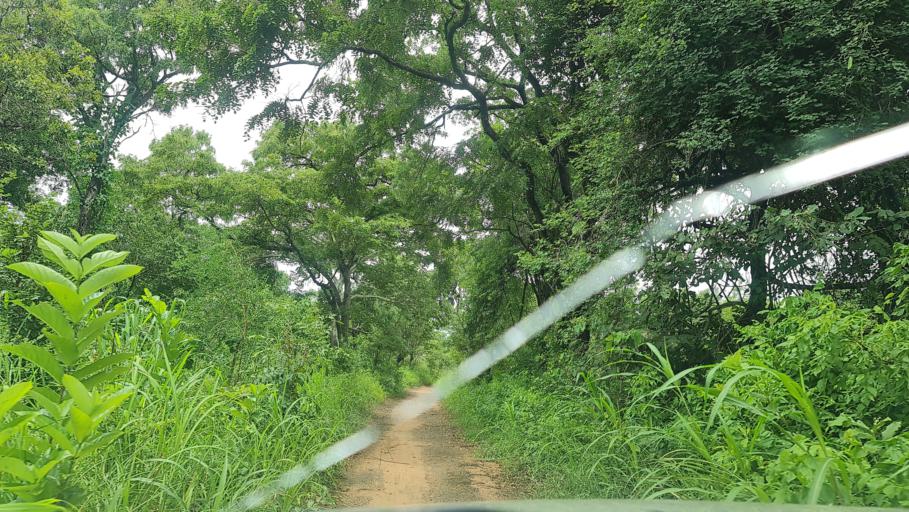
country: MW
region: Southern Region
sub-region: Nsanje District
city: Nsanje
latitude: -17.3783
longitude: 35.7754
